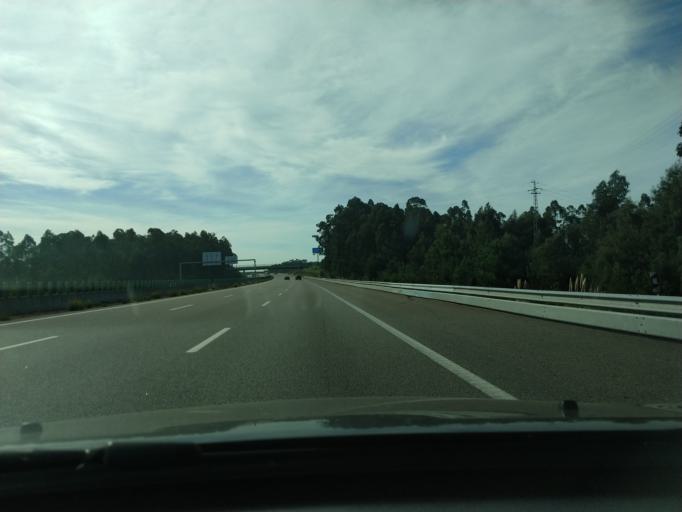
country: PT
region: Aveiro
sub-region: Santa Maria da Feira
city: Feira
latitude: 40.9157
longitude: -8.5680
